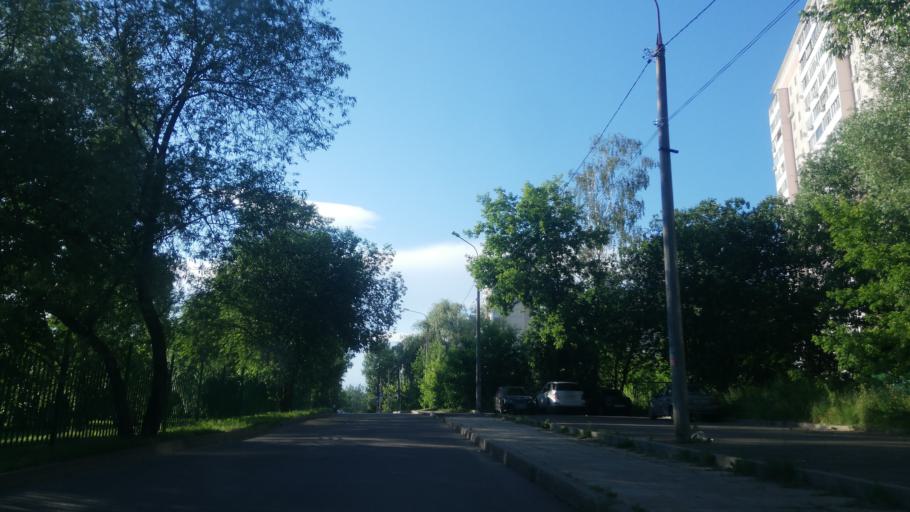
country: RU
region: Moskovskaya
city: Dolgoprudnyy
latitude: 55.9383
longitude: 37.4874
